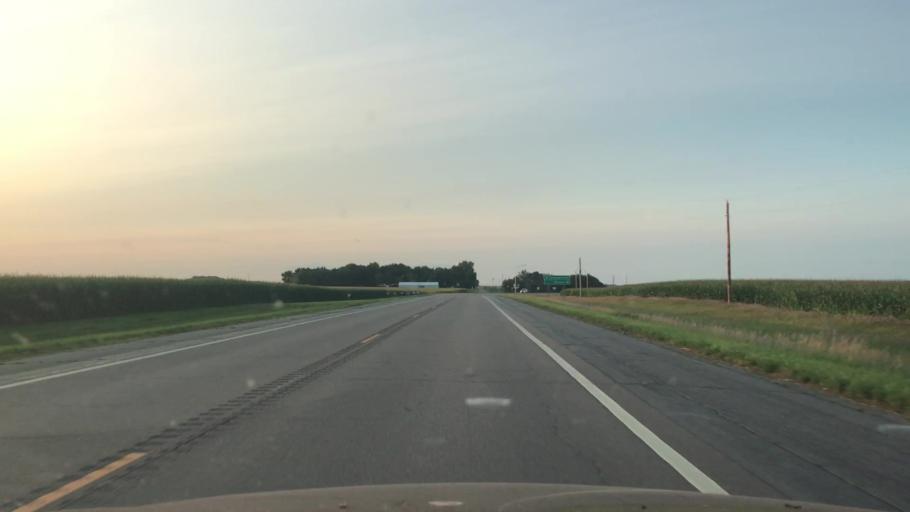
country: US
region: Minnesota
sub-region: Redwood County
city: Redwood Falls
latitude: 44.4096
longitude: -95.1276
